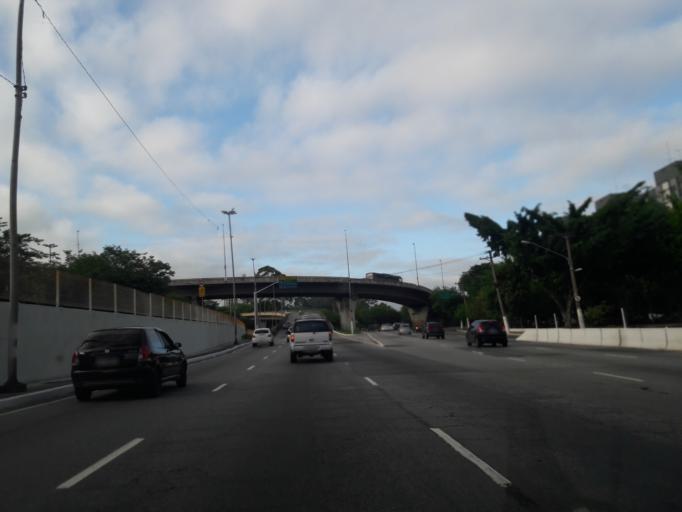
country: BR
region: Sao Paulo
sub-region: Sao Caetano Do Sul
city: Sao Caetano do Sul
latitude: -23.6016
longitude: -46.5992
